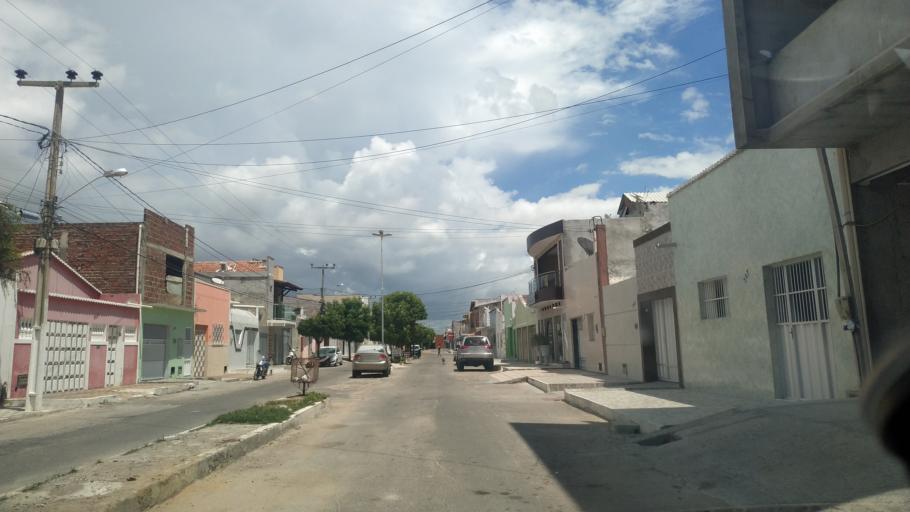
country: BR
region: Rio Grande do Norte
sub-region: Areia Branca
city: Areia Branca
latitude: -4.9541
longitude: -37.1345
